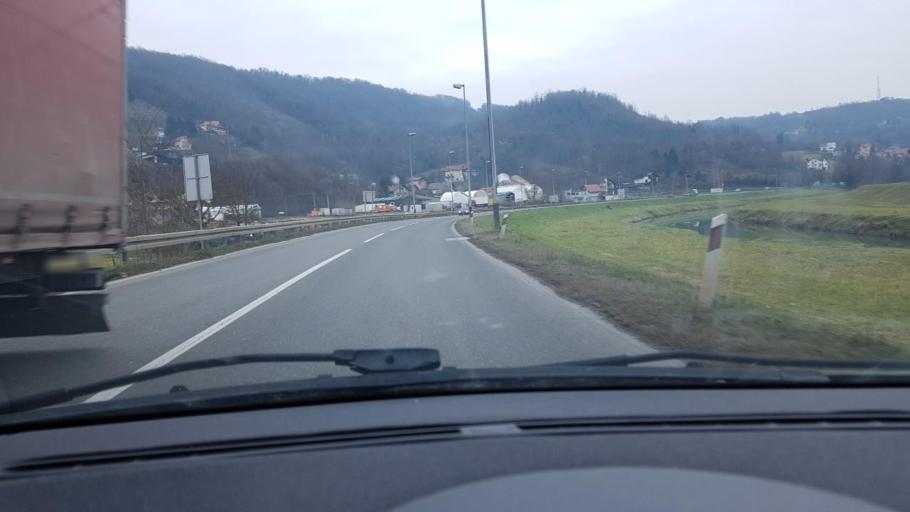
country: HR
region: Zagrebacka
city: Zapresic
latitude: 45.8451
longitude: 15.8290
